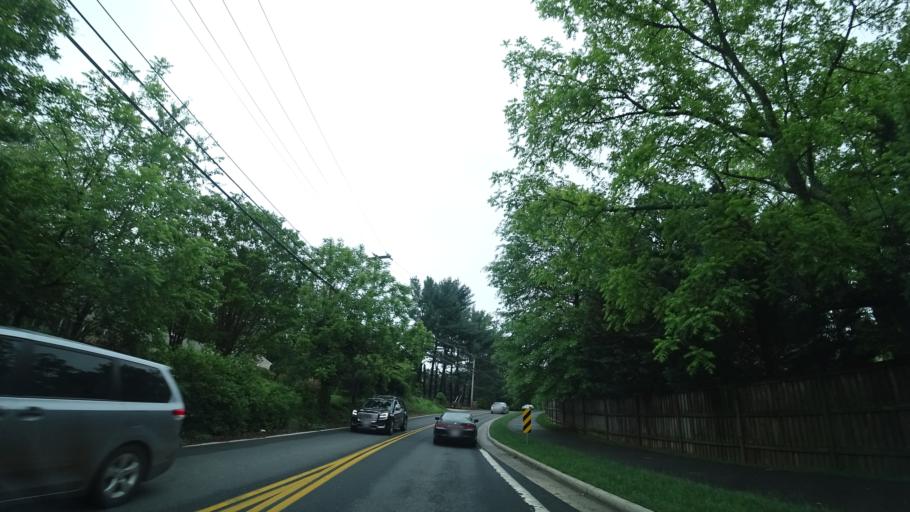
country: US
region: Virginia
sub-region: Fairfax County
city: Tysons Corner
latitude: 38.9415
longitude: -77.2486
